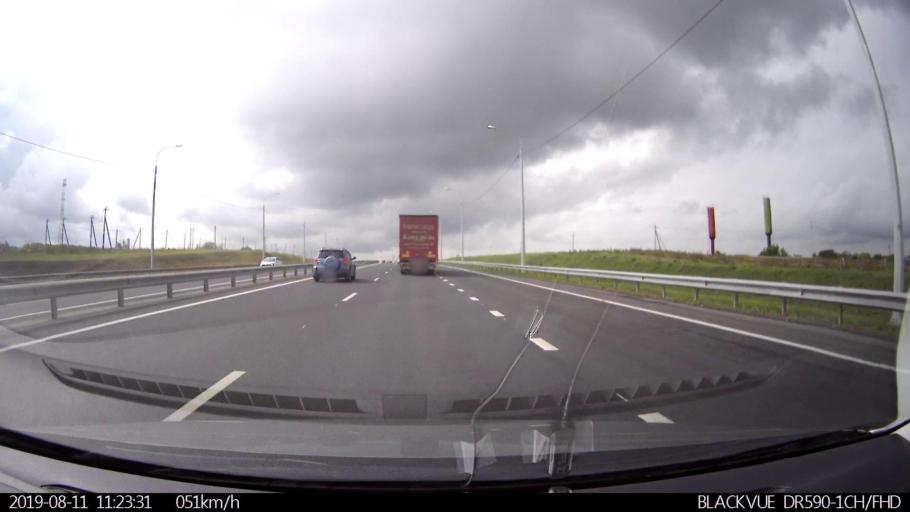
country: RU
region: Ulyanovsk
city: Krasnyy Gulyay
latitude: 54.1363
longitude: 48.2513
